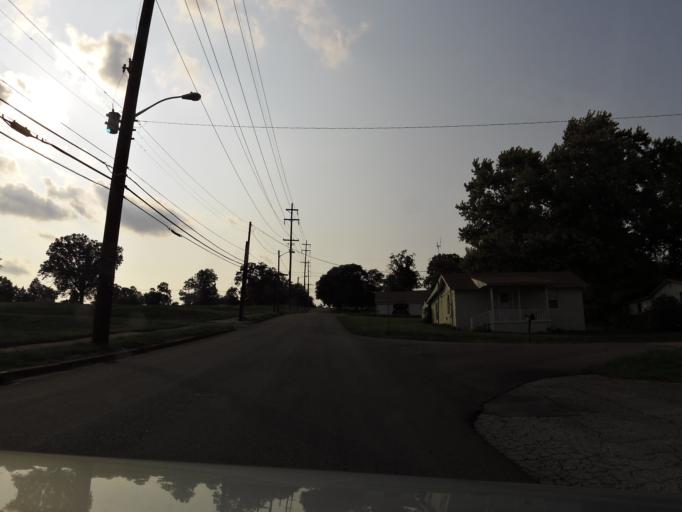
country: US
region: Tennessee
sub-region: Knox County
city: Knoxville
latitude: 35.9791
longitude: -83.9433
